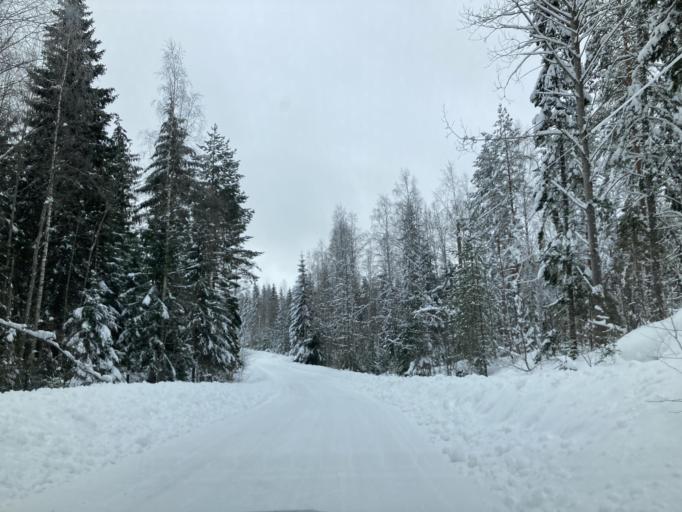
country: FI
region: Central Finland
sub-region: Jaemsae
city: Jaemsae
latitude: 61.8790
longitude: 25.3204
